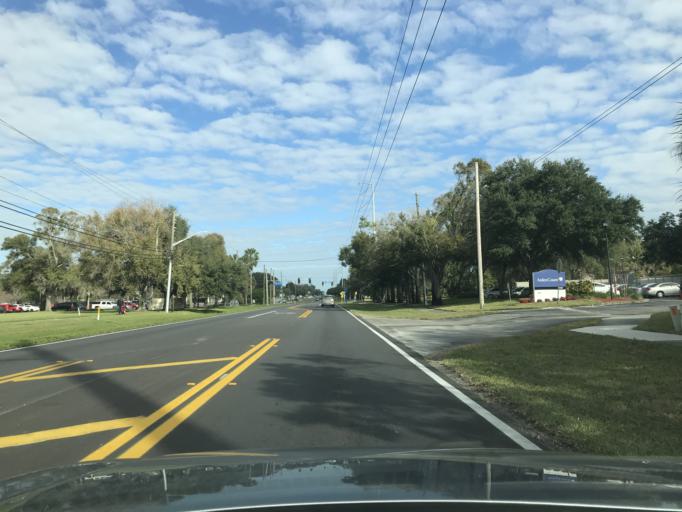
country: US
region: Florida
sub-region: Pinellas County
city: Largo
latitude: 27.9192
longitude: -82.7749
